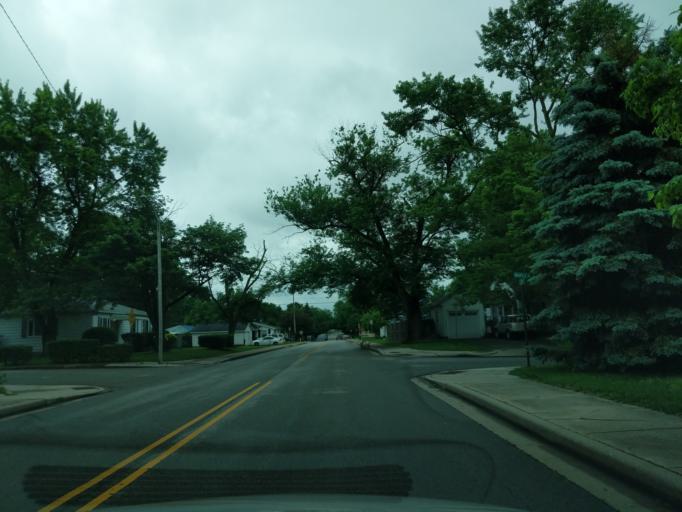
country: US
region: Indiana
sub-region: Hamilton County
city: Noblesville
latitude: 40.0449
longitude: -86.0003
